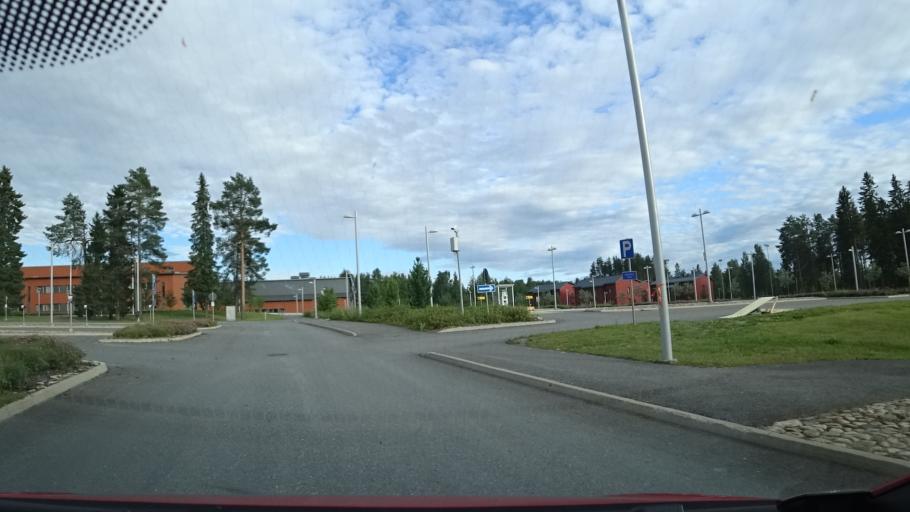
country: FI
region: Northern Ostrobothnia
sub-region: Oulu
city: Haukipudas
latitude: 65.1963
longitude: 25.4121
